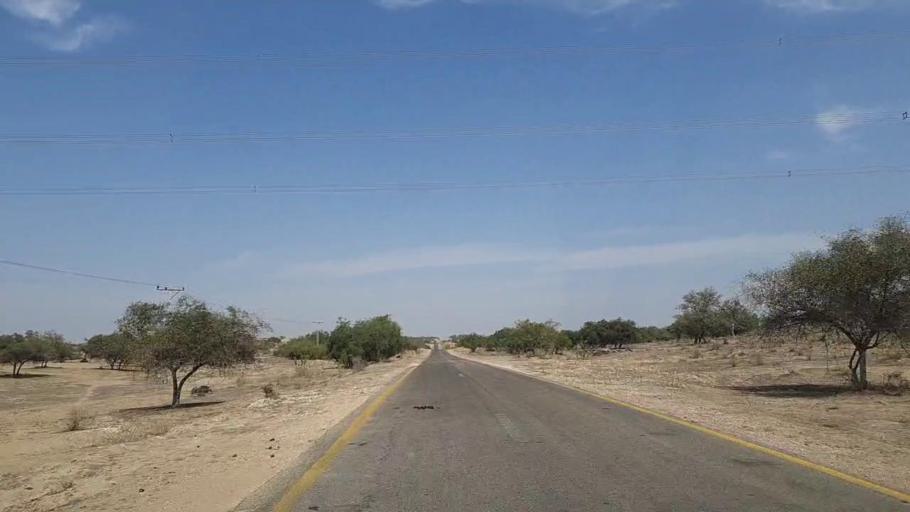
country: PK
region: Sindh
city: Mithi
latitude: 24.8525
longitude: 69.8385
